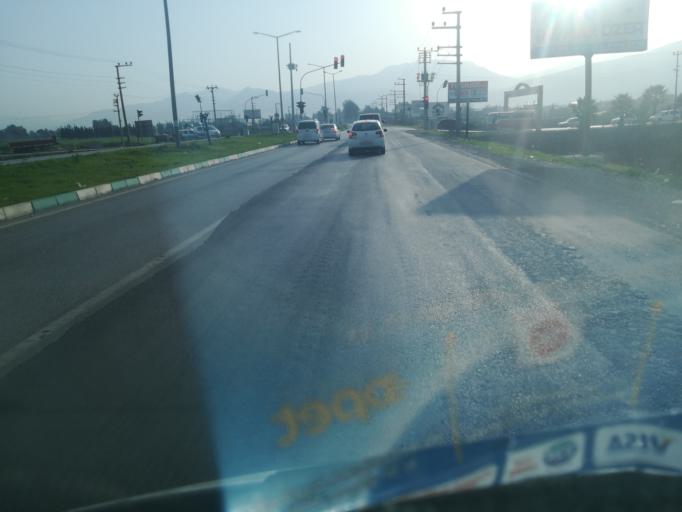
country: TR
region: Osmaniye
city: Osmaniye
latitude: 37.0561
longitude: 36.2000
